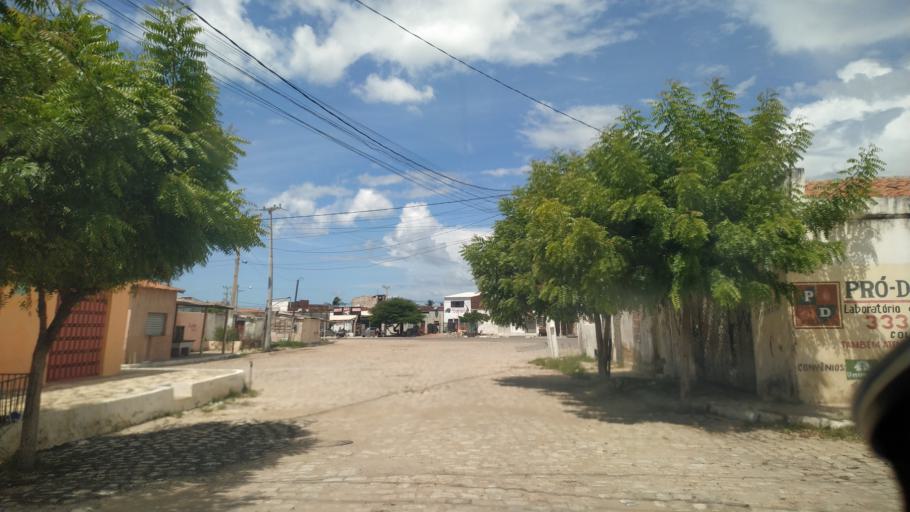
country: BR
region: Rio Grande do Norte
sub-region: Areia Branca
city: Areia Branca
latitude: -4.9540
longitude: -37.1301
